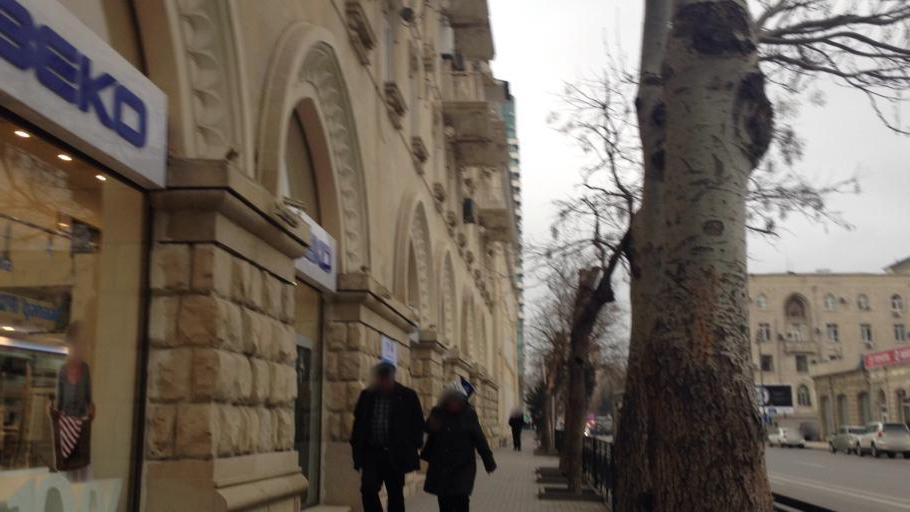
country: AZ
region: Baki
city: Baku
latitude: 40.3791
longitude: 49.8574
